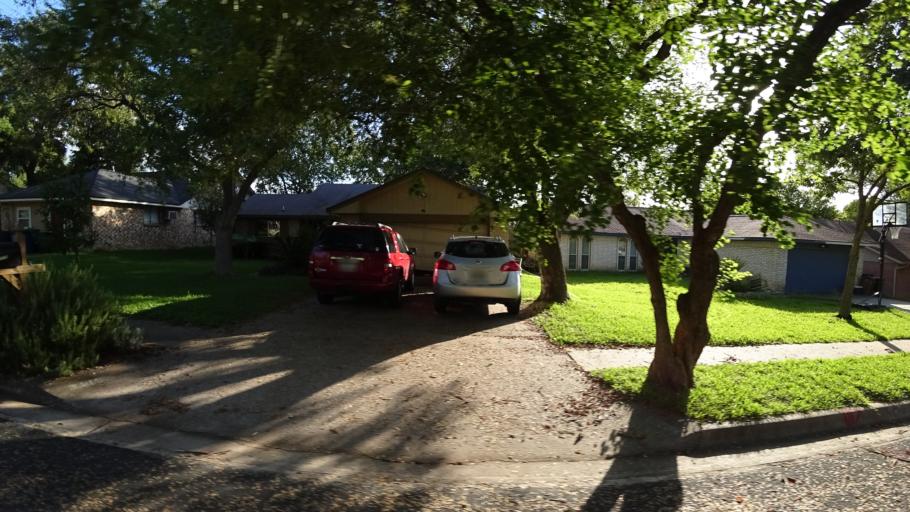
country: US
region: Texas
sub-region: Travis County
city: Onion Creek
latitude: 30.1983
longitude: -97.7968
